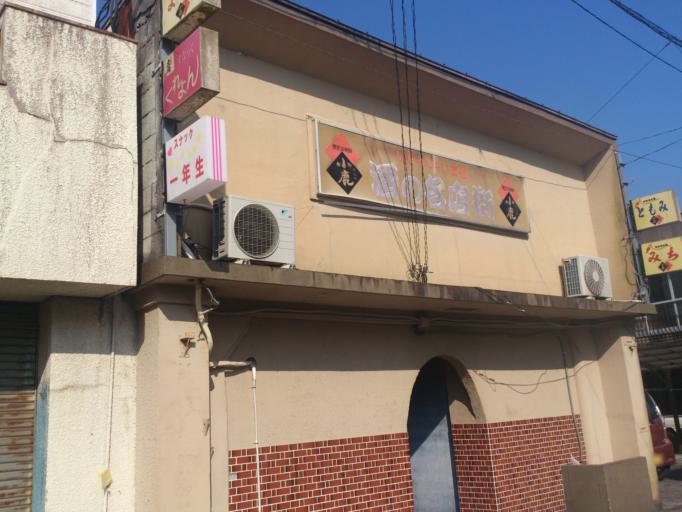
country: JP
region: Kagoshima
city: Kanoya
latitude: 31.3478
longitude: 130.9424
